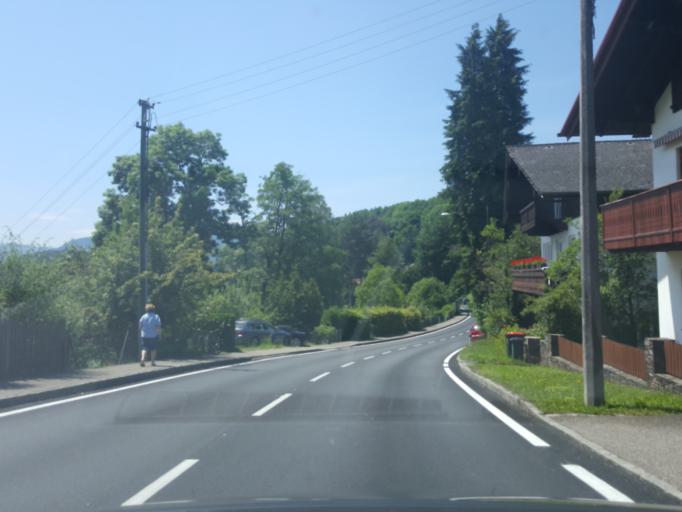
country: AT
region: Upper Austria
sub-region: Politischer Bezirk Vocklabruck
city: Seewalchen
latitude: 47.9504
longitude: 13.5791
